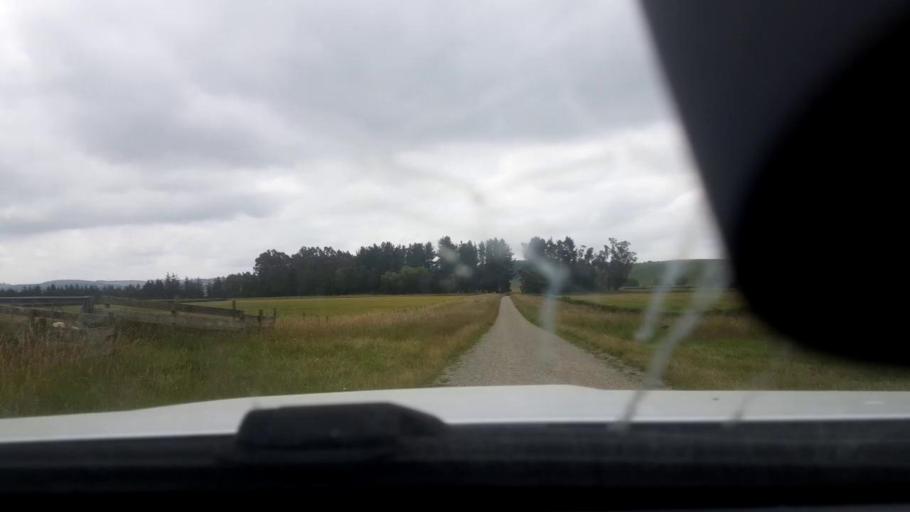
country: NZ
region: Canterbury
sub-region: Timaru District
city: Pleasant Point
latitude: -44.2236
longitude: 171.1637
